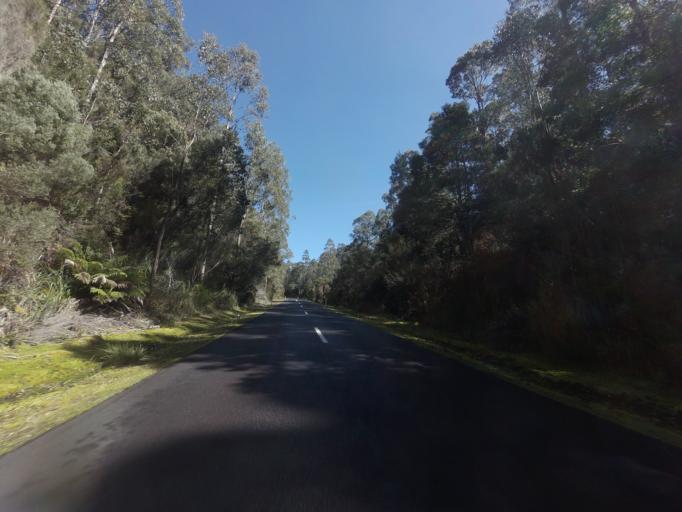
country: AU
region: Tasmania
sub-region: Derwent Valley
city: New Norfolk
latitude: -42.7331
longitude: 146.4748
